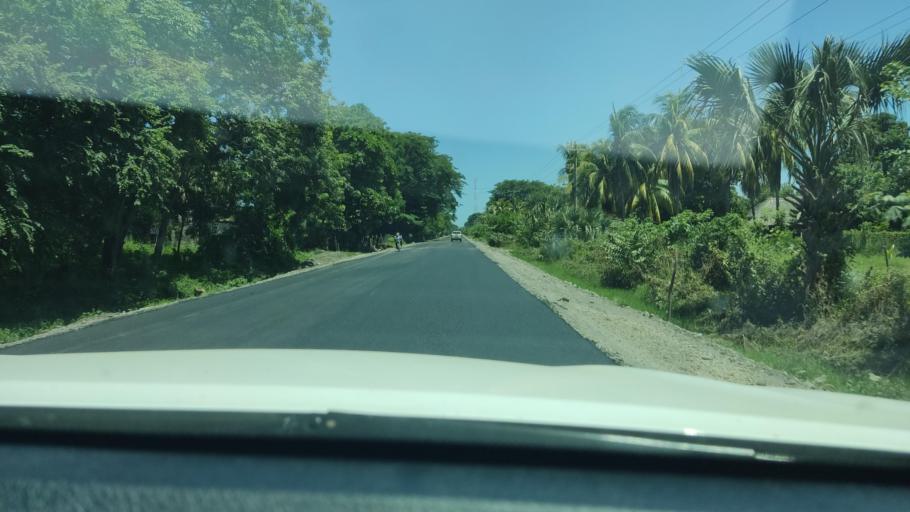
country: SV
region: Ahuachapan
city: San Francisco Menendez
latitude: 13.8341
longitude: -90.1196
